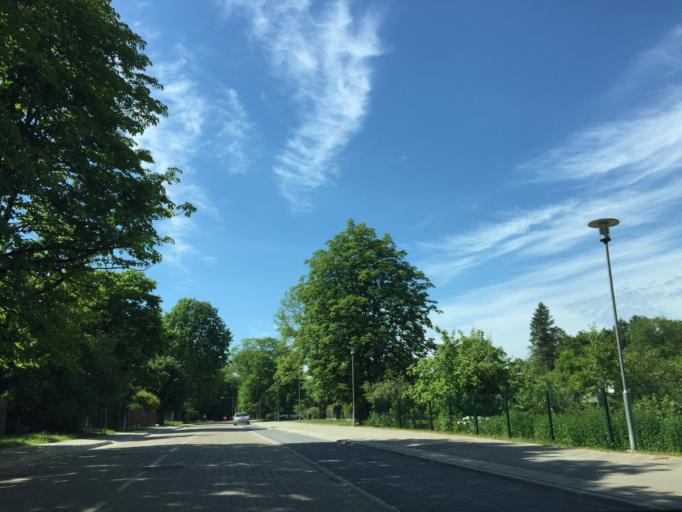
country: LV
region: Sigulda
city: Sigulda
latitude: 57.1626
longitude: 24.8488
